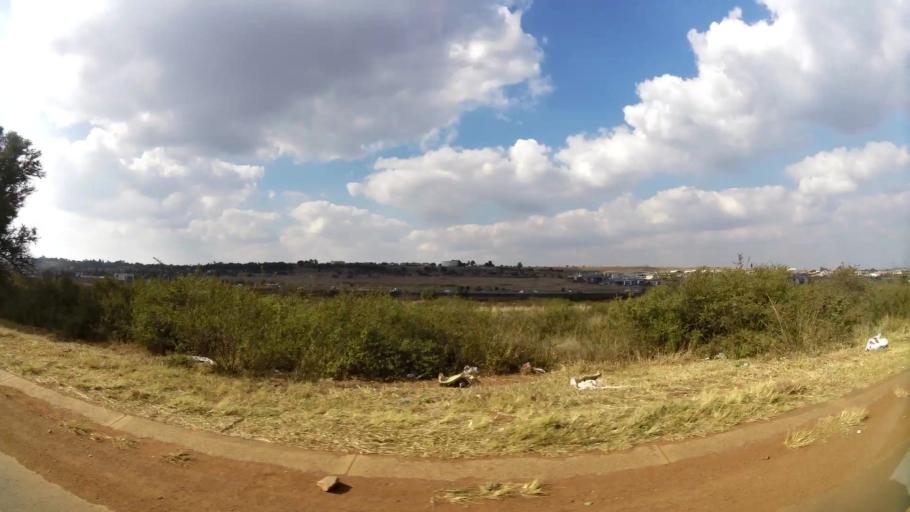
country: ZA
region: Gauteng
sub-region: City of Tshwane Metropolitan Municipality
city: Centurion
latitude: -25.8566
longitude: 28.2476
